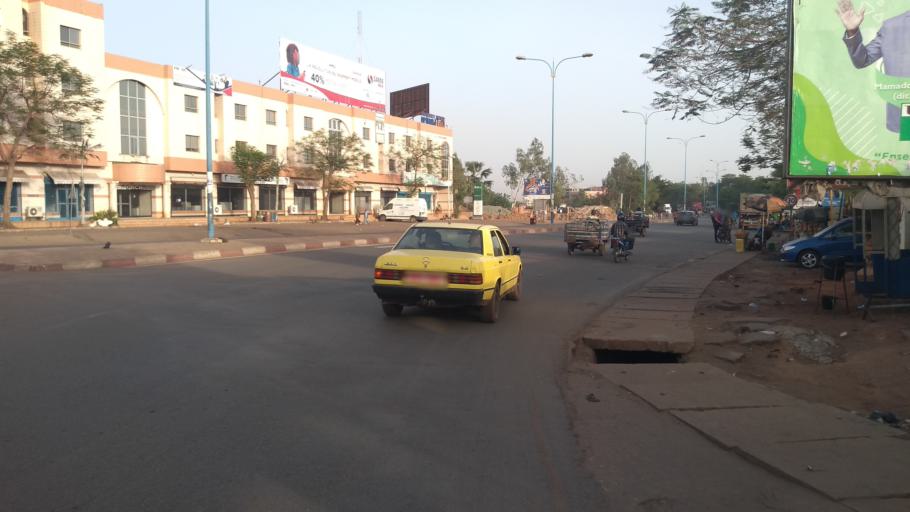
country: ML
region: Bamako
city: Bamako
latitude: 12.6420
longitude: -8.0209
